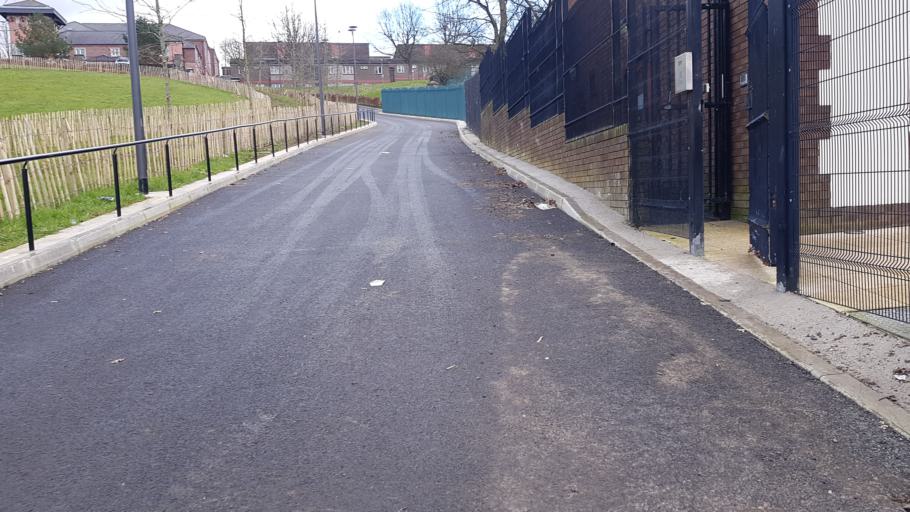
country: GB
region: Northern Ireland
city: Londonderry County Borough
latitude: 54.9940
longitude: -7.3278
